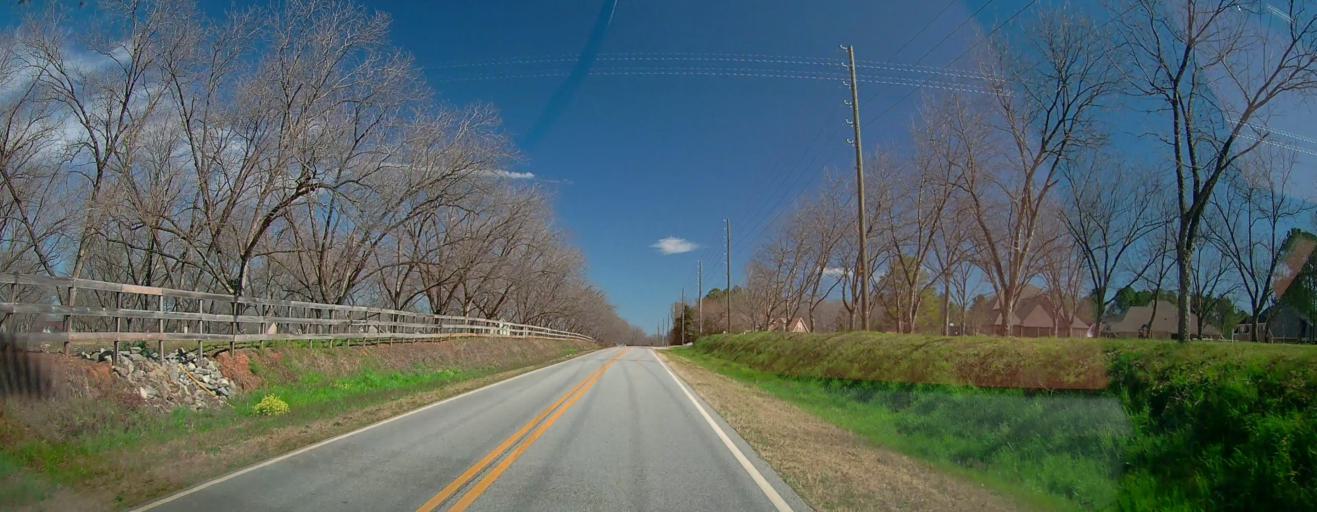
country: US
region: Georgia
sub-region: Houston County
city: Perry
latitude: 32.4899
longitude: -83.6488
